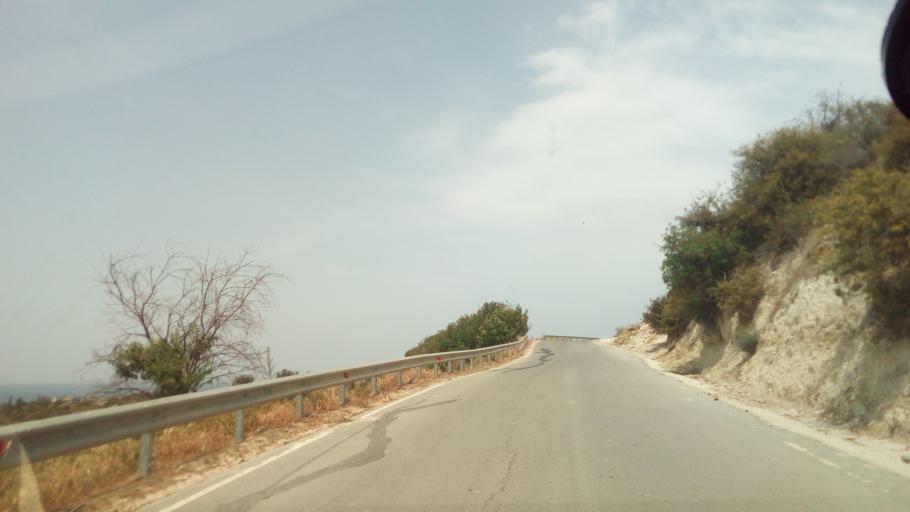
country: CY
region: Pafos
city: Polis
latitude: 35.0204
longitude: 32.4001
